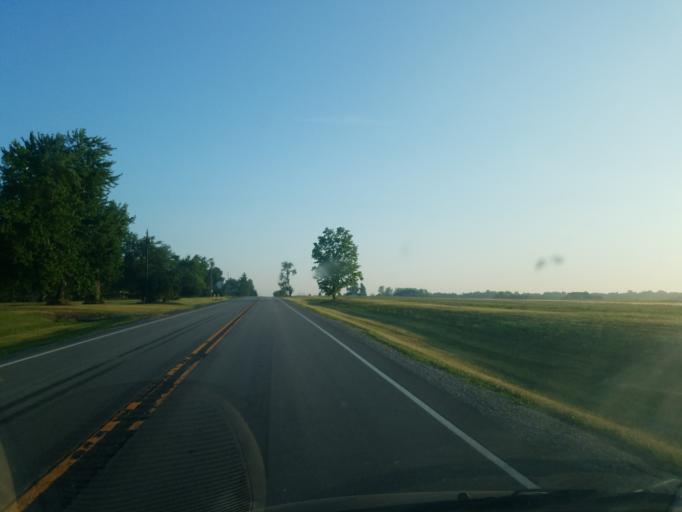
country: US
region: Indiana
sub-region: Allen County
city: Harlan
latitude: 41.2556
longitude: -84.8663
